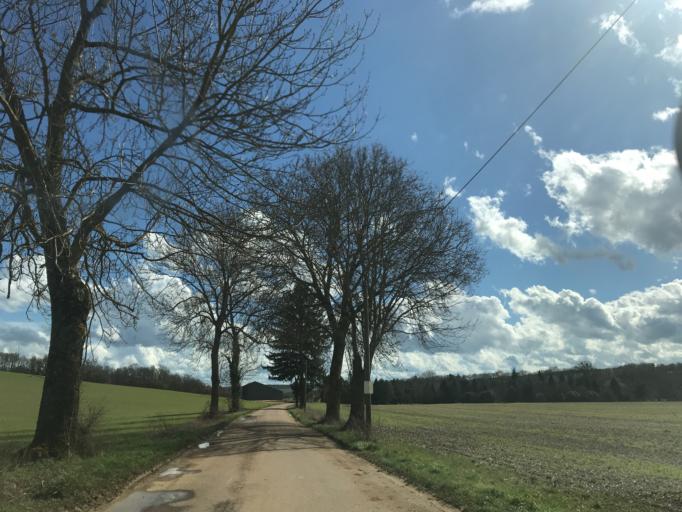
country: FR
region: Bourgogne
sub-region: Departement de l'Yonne
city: Fontenailles
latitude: 47.5152
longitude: 3.4953
